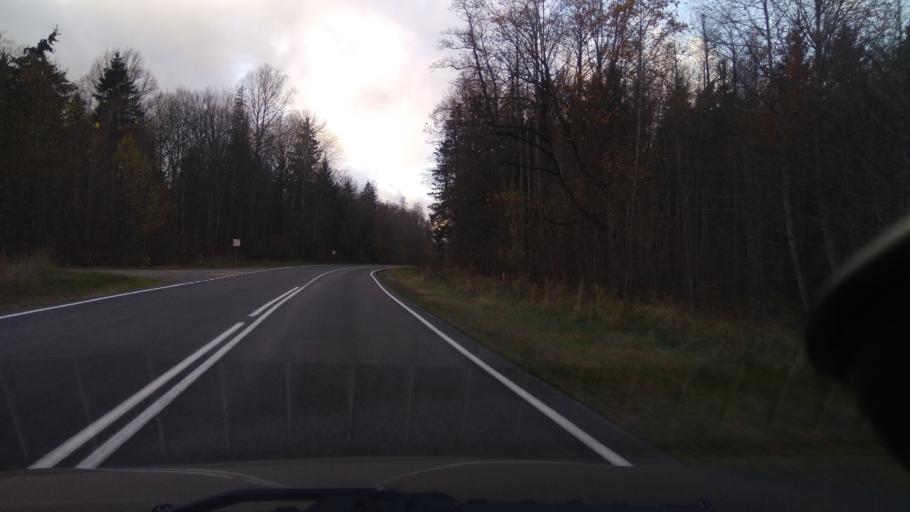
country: BY
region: Minsk
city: Urechcha
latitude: 53.2078
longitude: 27.9171
